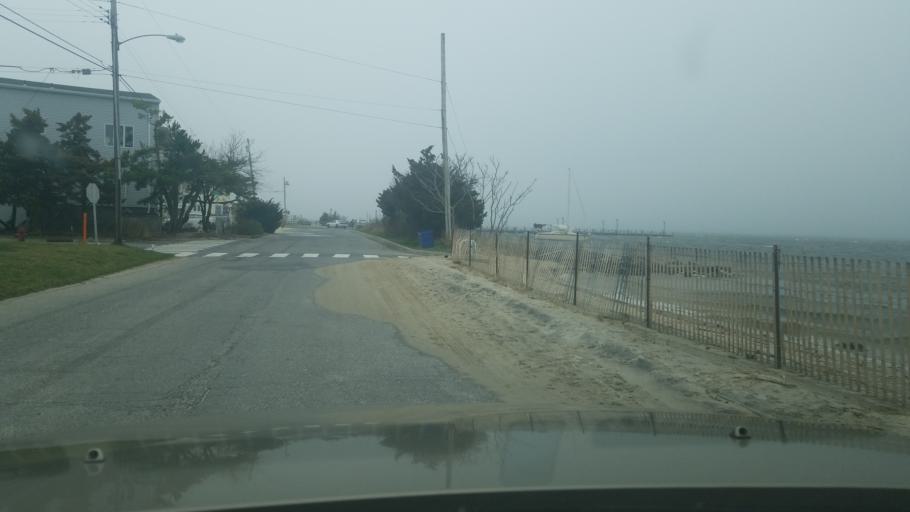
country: US
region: New Jersey
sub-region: Ocean County
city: Seaside Park
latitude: 39.9073
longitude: -74.0862
